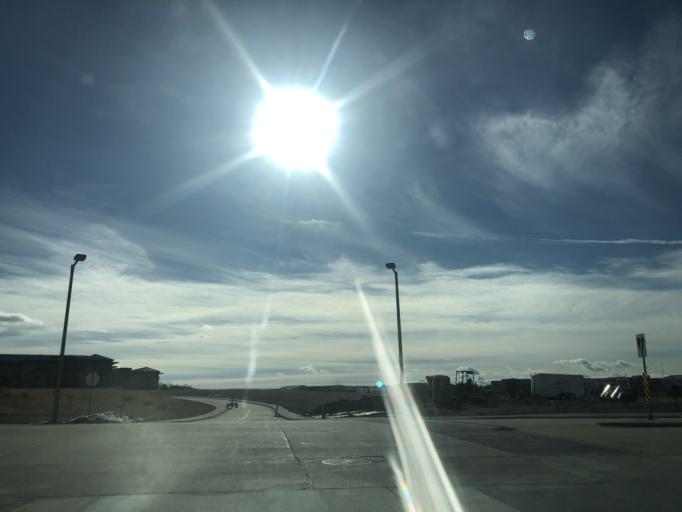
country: US
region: Colorado
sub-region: Douglas County
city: Meridian
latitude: 39.5489
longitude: -104.8585
